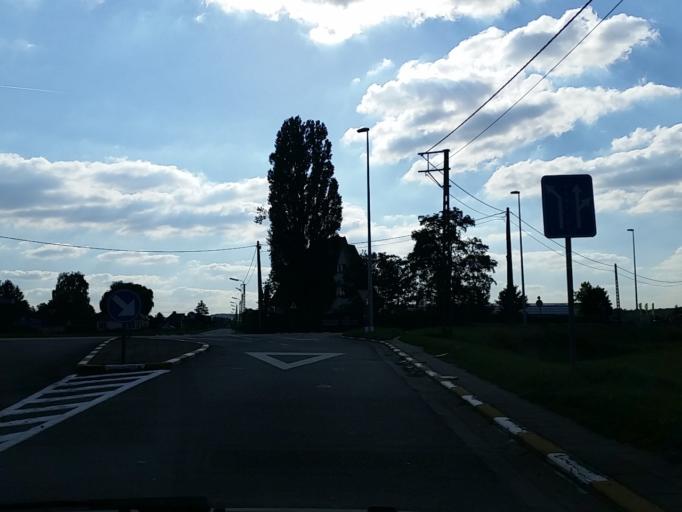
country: BE
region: Flanders
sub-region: Provincie Vlaams-Brabant
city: Bertem
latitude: 50.8959
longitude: 4.6104
